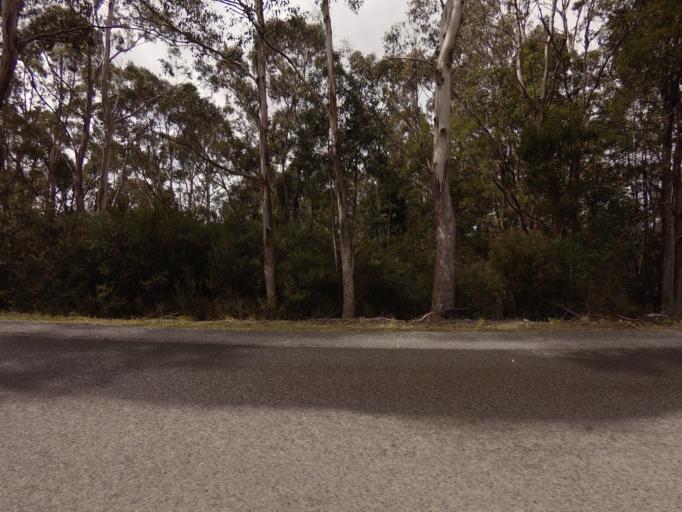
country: AU
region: Tasmania
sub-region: Huon Valley
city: Geeveston
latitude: -43.4402
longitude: 146.9038
